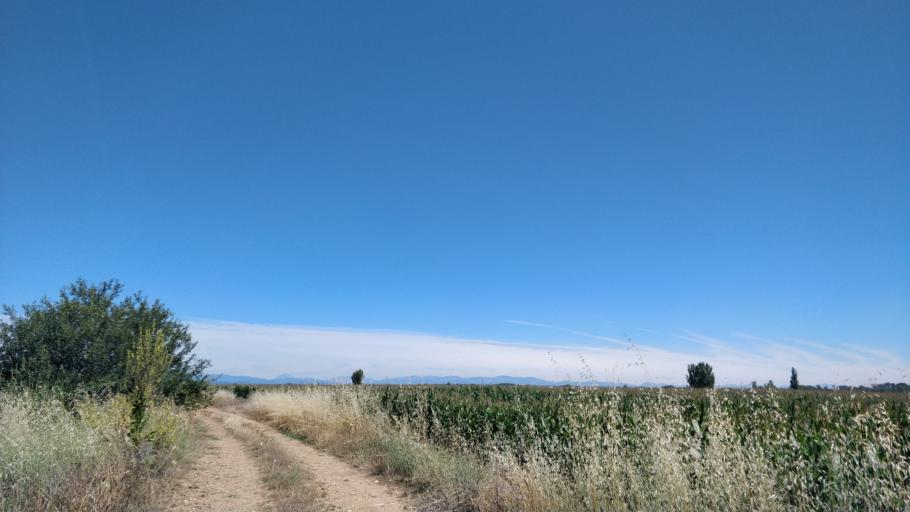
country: ES
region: Castille and Leon
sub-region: Provincia de Leon
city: Bustillo del Paramo
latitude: 42.4469
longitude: -5.8153
